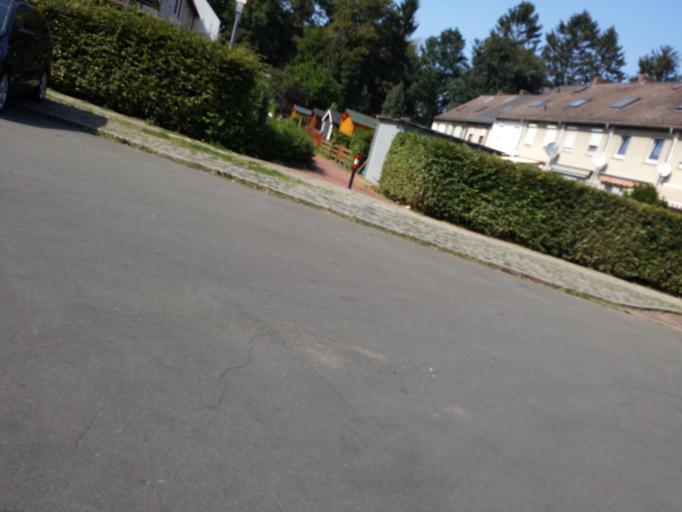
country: DE
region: Bremen
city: Bremen
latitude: 53.0257
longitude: 8.8178
